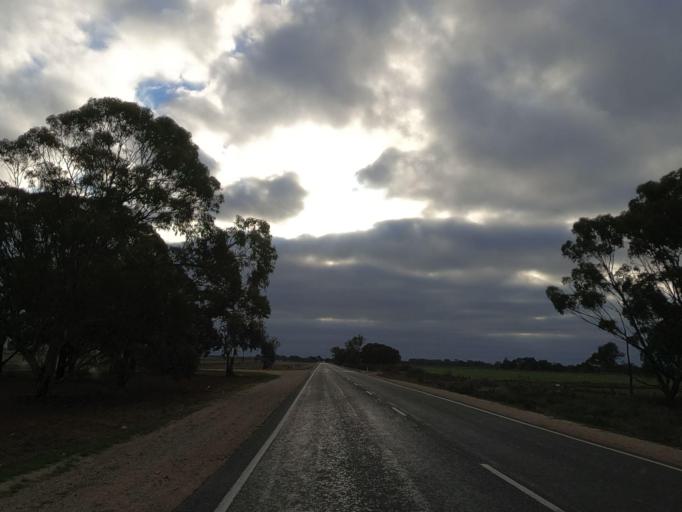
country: AU
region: Victoria
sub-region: Swan Hill
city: Swan Hill
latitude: -35.6558
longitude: 143.8507
